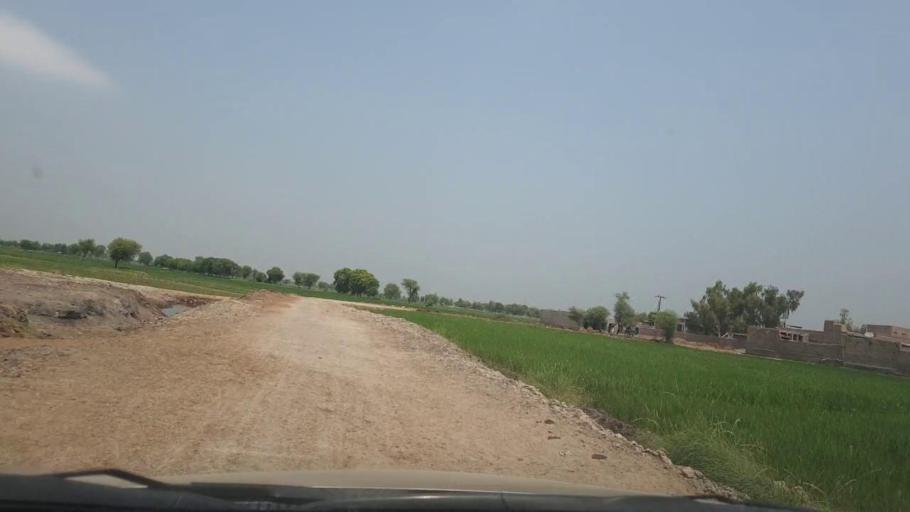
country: PK
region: Sindh
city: Ratodero
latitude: 27.7287
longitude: 68.2949
